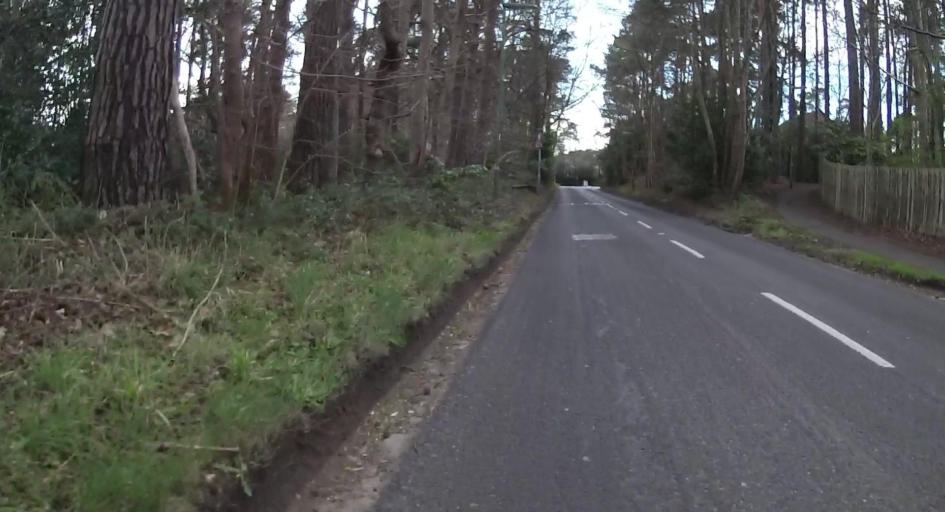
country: GB
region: England
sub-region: Surrey
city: Camberley
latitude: 51.3242
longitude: -0.7059
